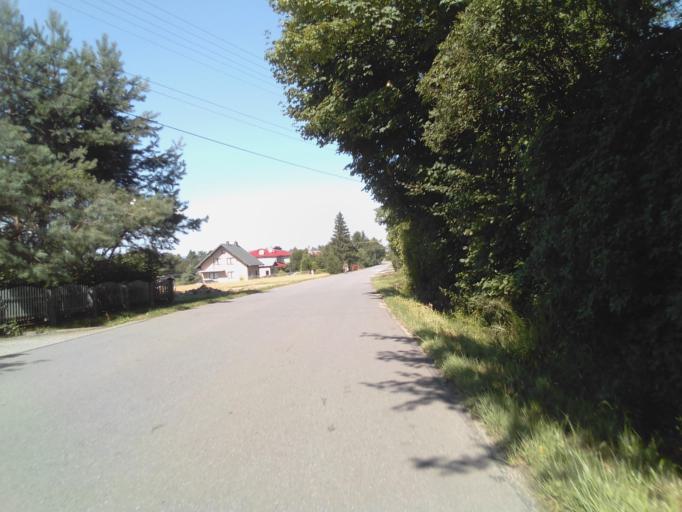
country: PL
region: Subcarpathian Voivodeship
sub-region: Powiat krosnienski
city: Chorkowka
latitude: 49.6057
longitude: 21.6551
